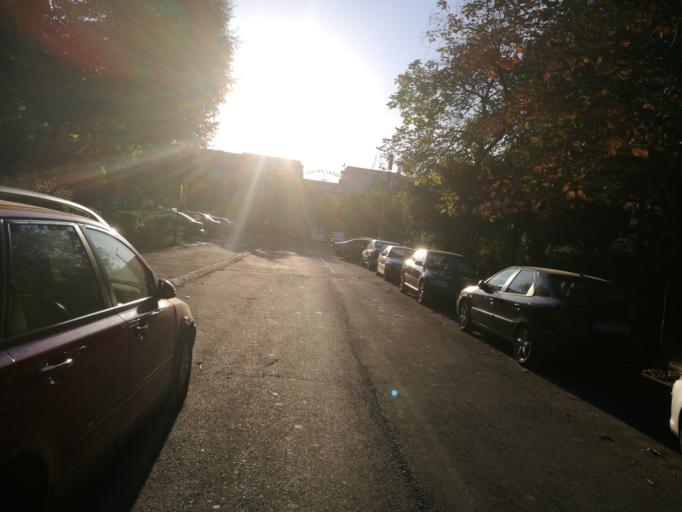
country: RO
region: Bucuresti
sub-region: Municipiul Bucuresti
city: Bucharest
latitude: 44.4843
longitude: 26.1006
